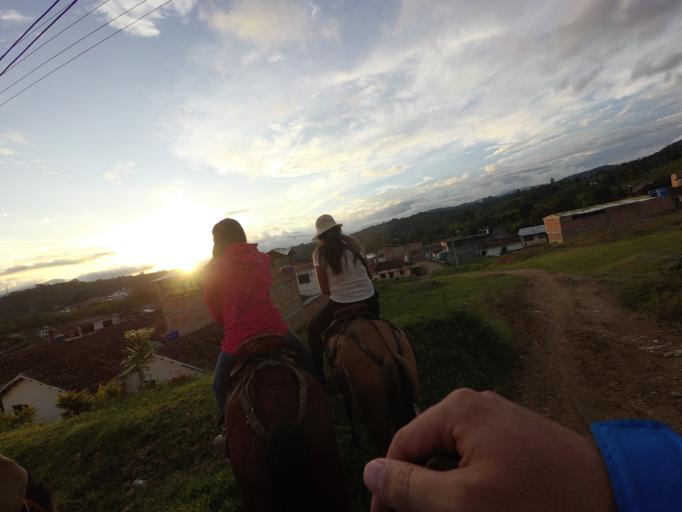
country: CO
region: Huila
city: San Agustin
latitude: 1.8857
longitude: -76.2728
